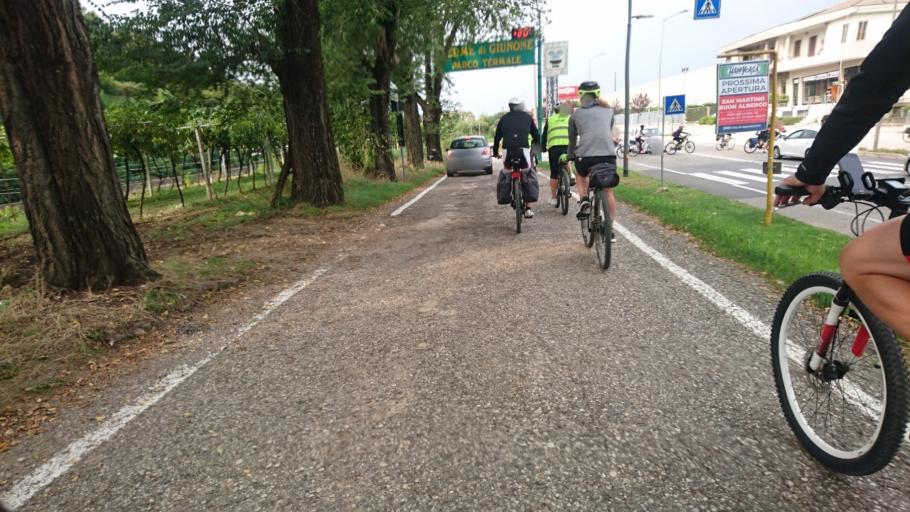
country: IT
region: Veneto
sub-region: Provincia di Verona
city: Caldiero
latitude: 45.4131
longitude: 11.1947
